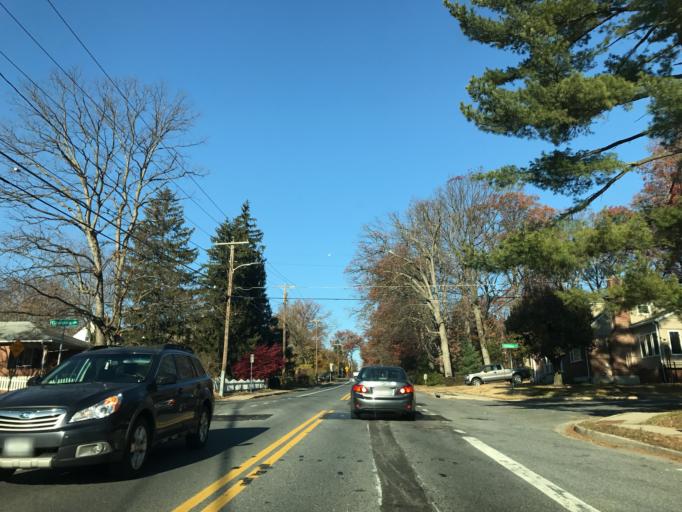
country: US
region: Maryland
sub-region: Baltimore County
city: Catonsville
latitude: 39.2607
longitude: -76.7347
